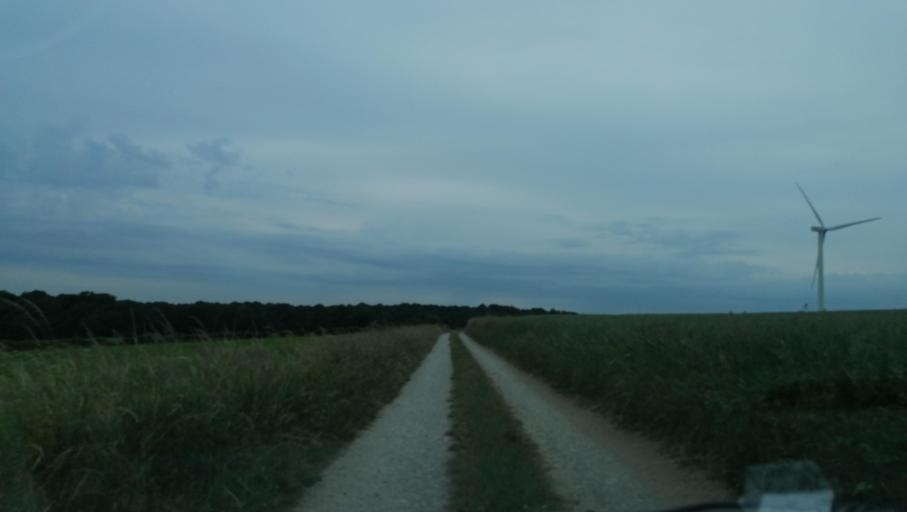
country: BE
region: Wallonia
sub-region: Province du Hainaut
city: Beaumont
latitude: 50.2072
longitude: 4.1621
